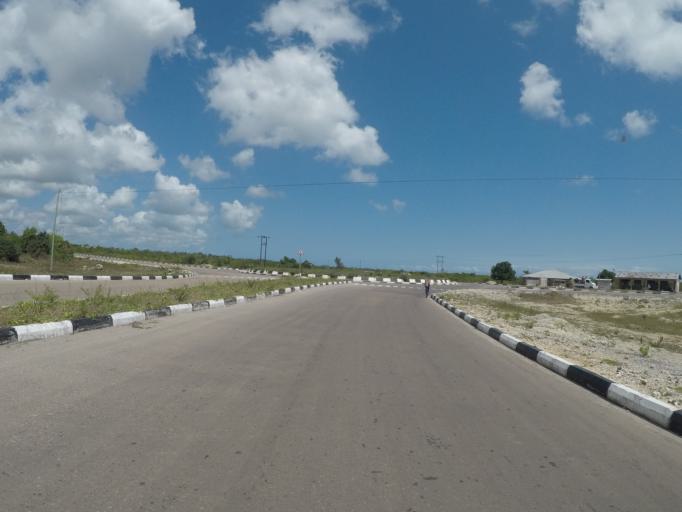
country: TZ
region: Zanzibar Central/South
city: Koani
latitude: -6.2774
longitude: 39.3655
